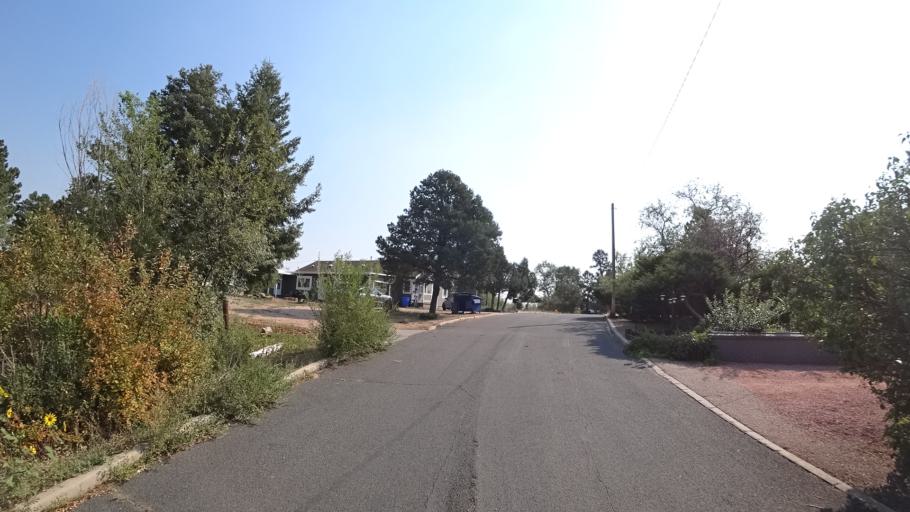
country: US
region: Colorado
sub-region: El Paso County
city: Colorado Springs
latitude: 38.8138
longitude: -104.8369
